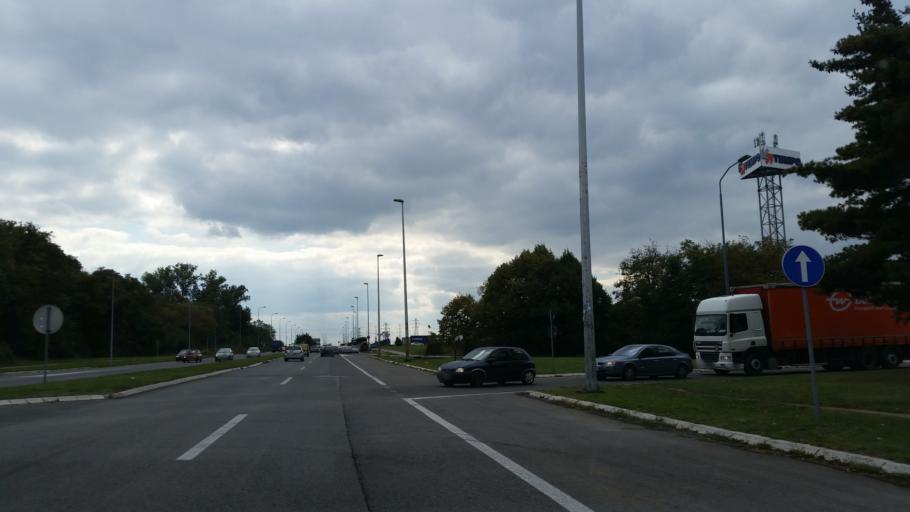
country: RS
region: Central Serbia
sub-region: Belgrade
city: Zemun
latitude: 44.8314
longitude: 20.3632
